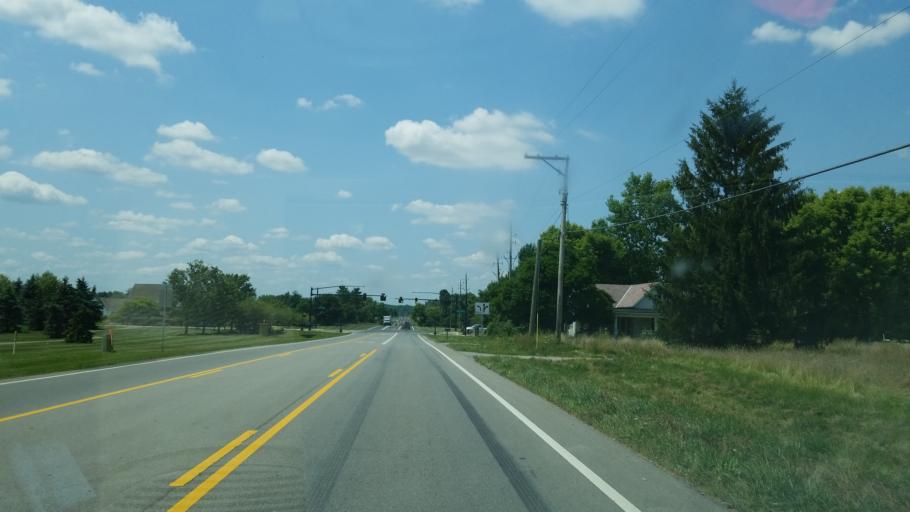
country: US
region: Ohio
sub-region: Delaware County
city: Powell
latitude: 40.1968
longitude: -83.1178
